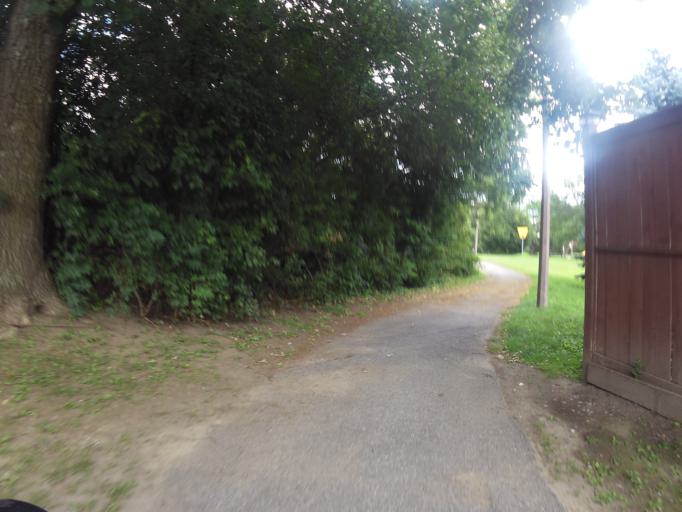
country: CA
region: Ontario
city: Bells Corners
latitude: 45.3186
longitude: -75.9078
